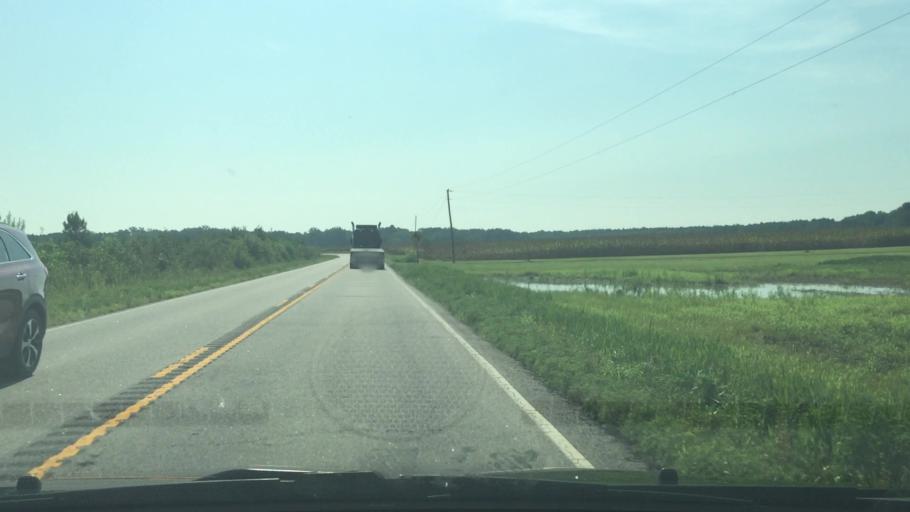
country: US
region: Virginia
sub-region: Sussex County
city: Sussex
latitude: 36.9784
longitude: -77.2293
